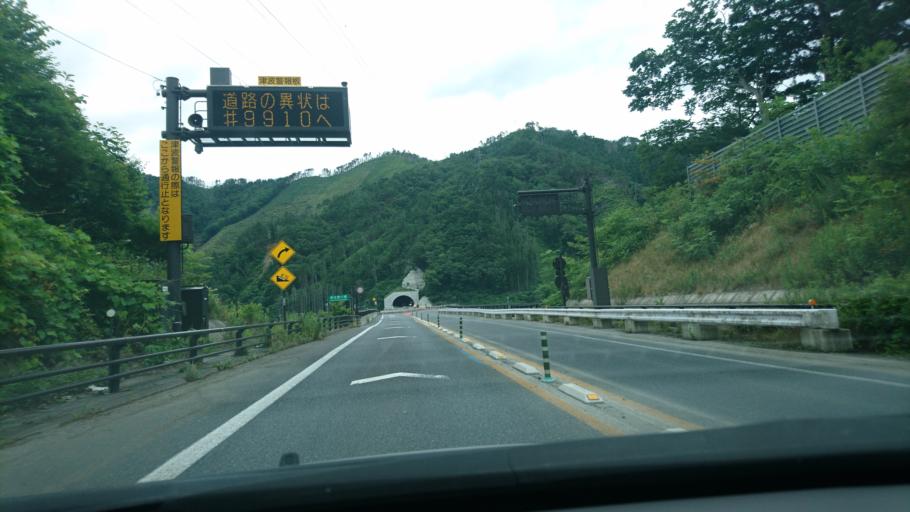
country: JP
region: Iwate
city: Otsuchi
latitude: 39.3339
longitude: 141.8791
